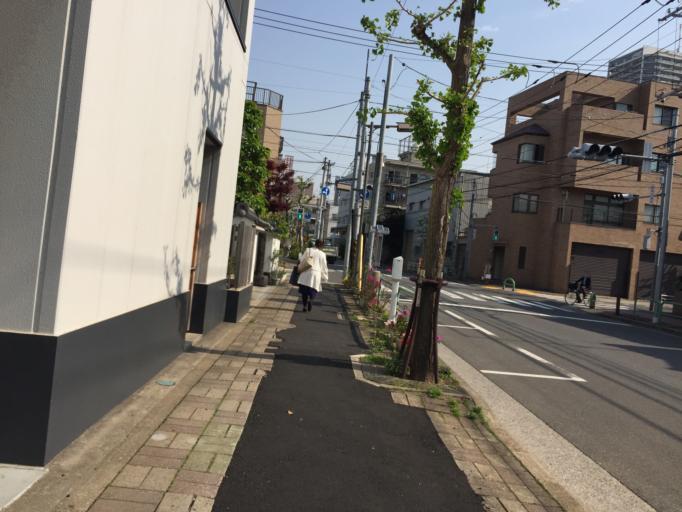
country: JP
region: Tokyo
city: Urayasu
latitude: 35.6799
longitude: 139.8037
